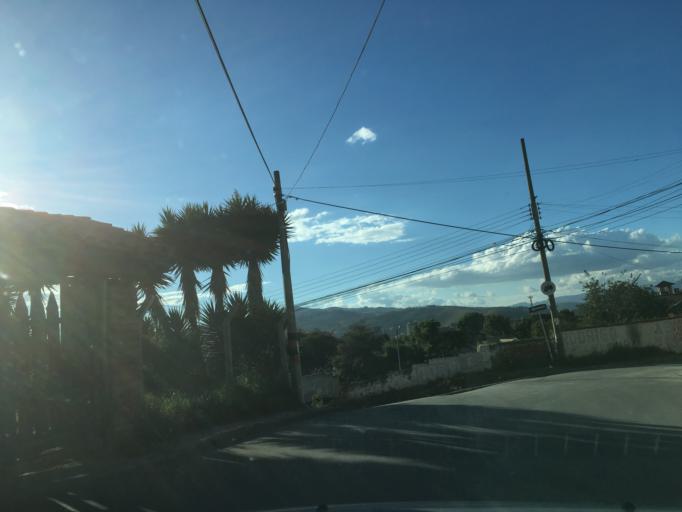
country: CO
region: Boyaca
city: Sogamoso
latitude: 5.7103
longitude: -72.9254
